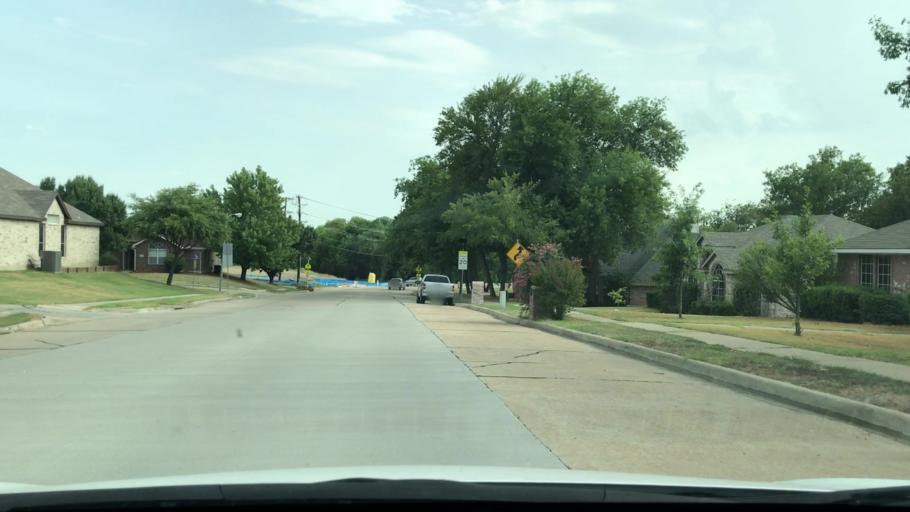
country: US
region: Texas
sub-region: Collin County
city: Wylie
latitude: 33.0124
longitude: -96.5202
